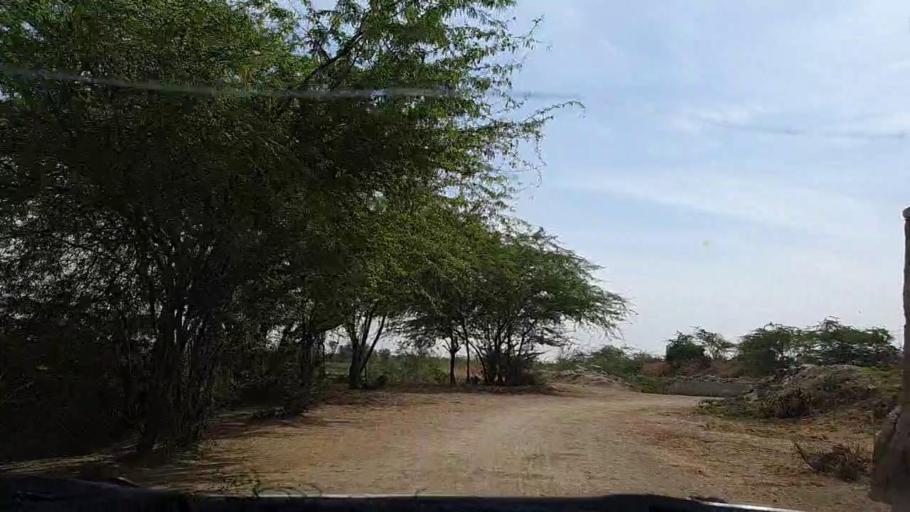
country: PK
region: Sindh
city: Pithoro
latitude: 25.4806
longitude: 69.4366
